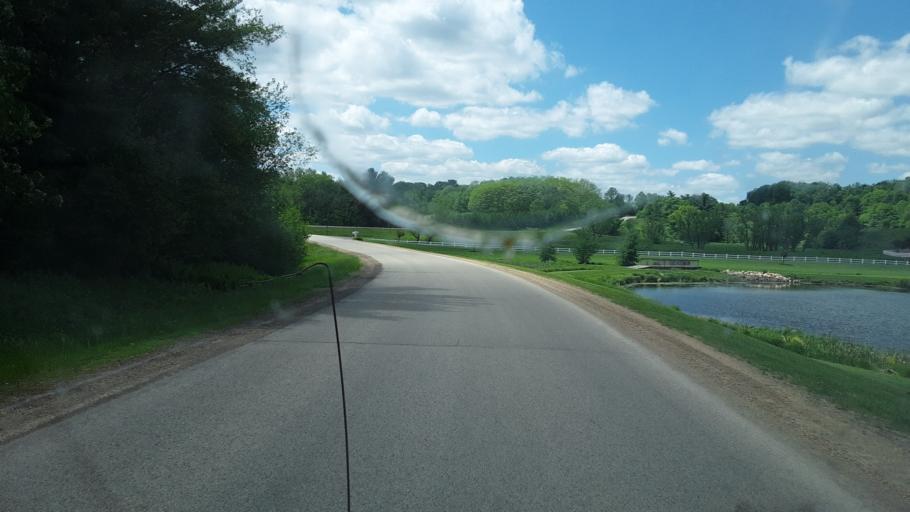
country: US
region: Wisconsin
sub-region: Sauk County
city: Reedsburg
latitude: 43.5767
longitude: -90.0405
